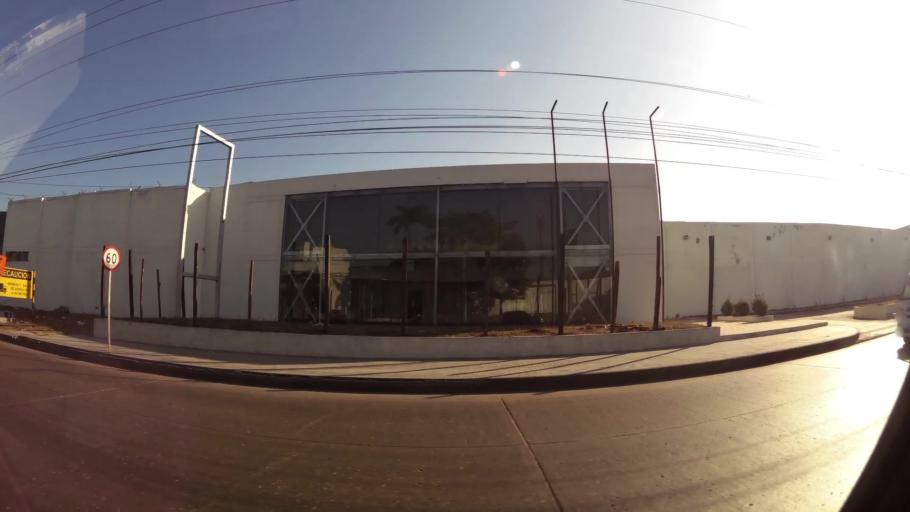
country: CO
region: Atlantico
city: Barranquilla
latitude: 11.0137
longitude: -74.7936
